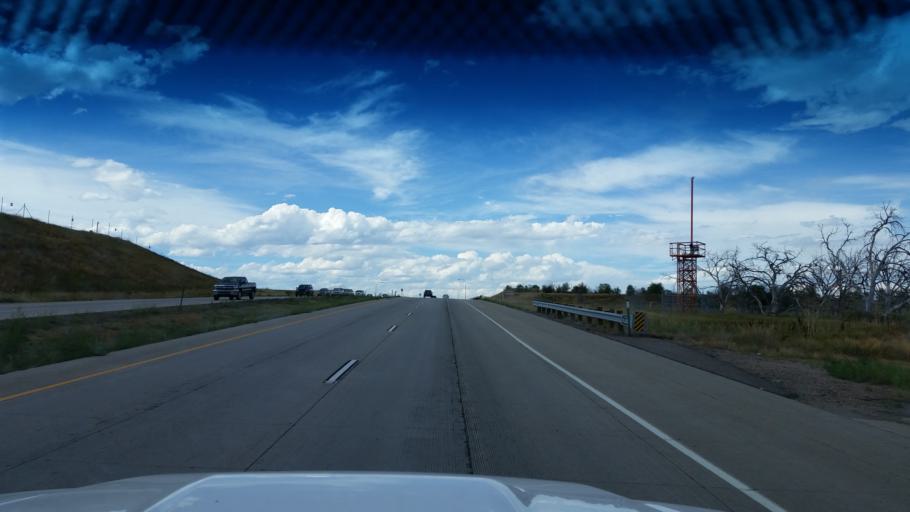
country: US
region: Colorado
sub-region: Broomfield County
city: Broomfield
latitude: 39.8974
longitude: -105.0959
